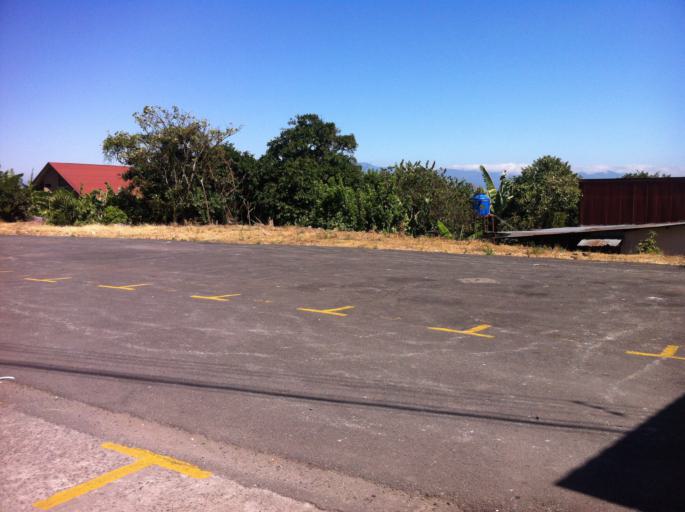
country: CR
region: San Jose
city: San Juan de Dios
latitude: 9.8775
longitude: -84.0849
